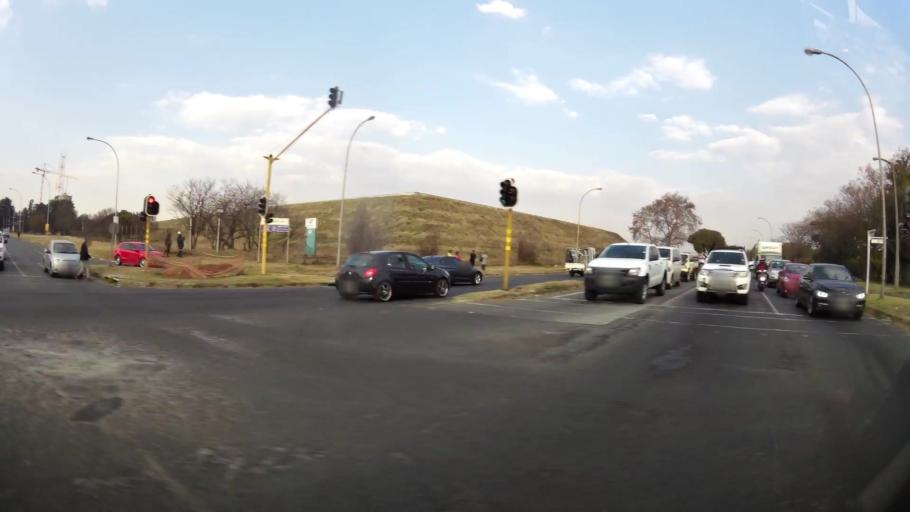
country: ZA
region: Gauteng
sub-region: Ekurhuleni Metropolitan Municipality
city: Benoni
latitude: -26.1623
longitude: 28.3063
